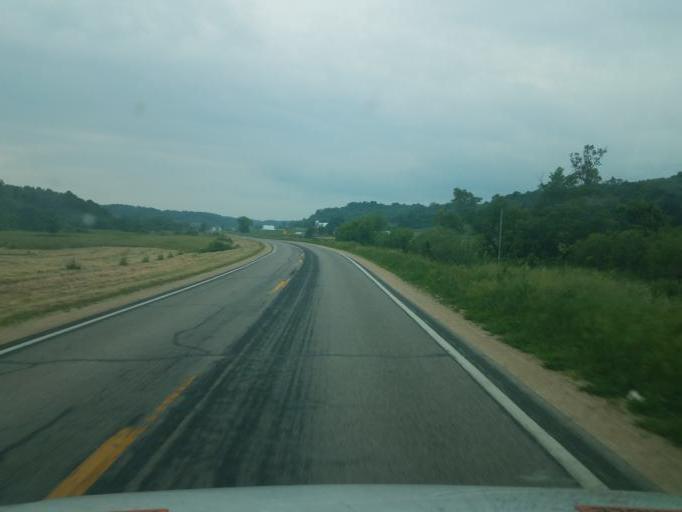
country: US
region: Wisconsin
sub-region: Vernon County
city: Hillsboro
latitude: 43.6537
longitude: -90.3948
